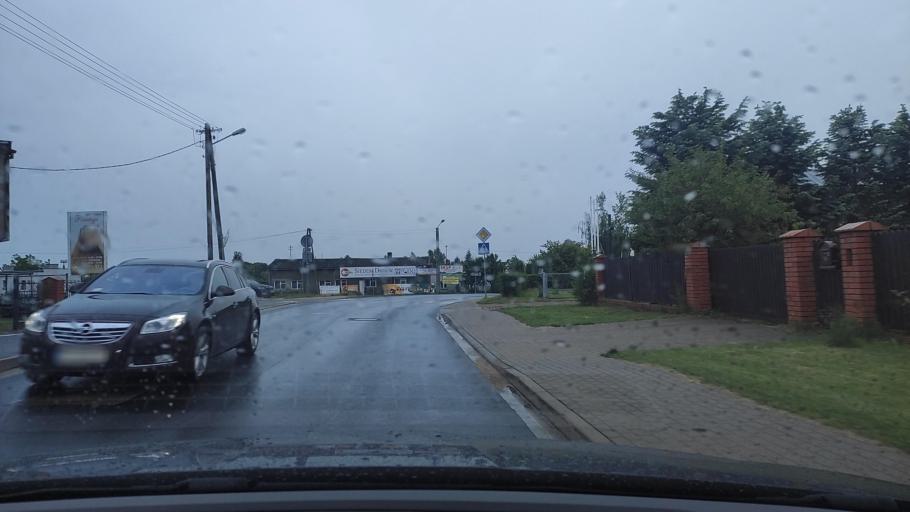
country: PL
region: Greater Poland Voivodeship
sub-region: Powiat poznanski
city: Kostrzyn
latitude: 52.4627
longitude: 17.1690
